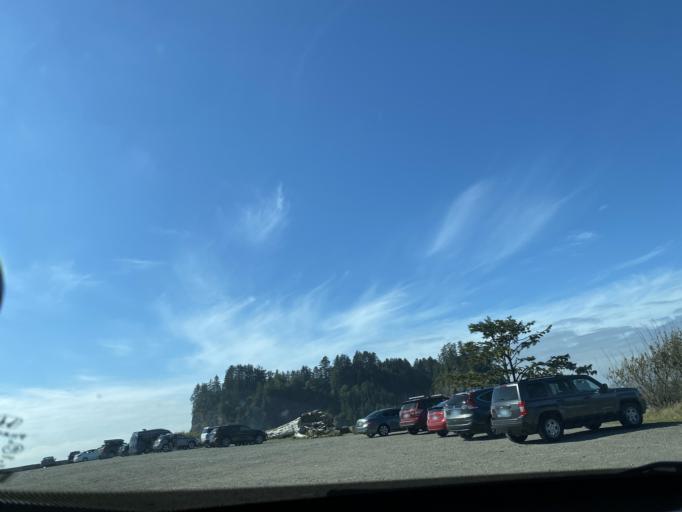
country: US
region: Washington
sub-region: Clallam County
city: Forks
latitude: 47.9088
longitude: -124.6392
